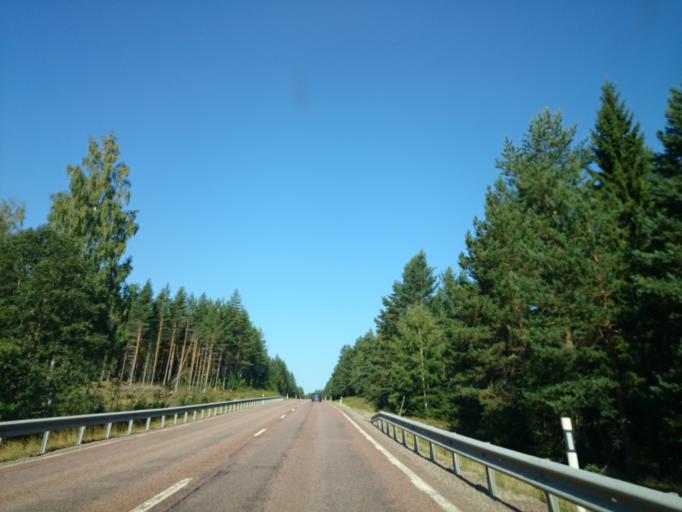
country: SE
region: Gaevleborg
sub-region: Hudiksvalls Kommun
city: Sorforsa
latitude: 61.7537
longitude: 16.8235
